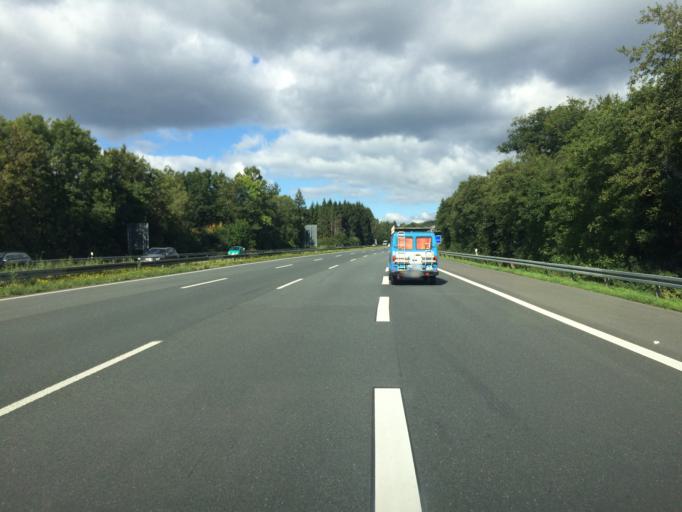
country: DE
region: Hesse
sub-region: Regierungsbezirk Giessen
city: Haiger
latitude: 50.7662
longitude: 8.1514
